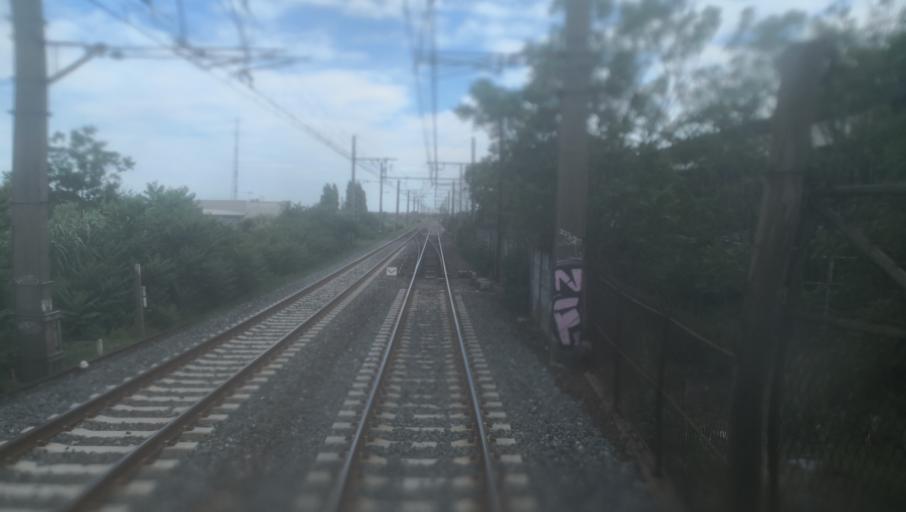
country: FR
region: Languedoc-Roussillon
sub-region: Departement de l'Herault
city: Frontignan
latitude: 43.4414
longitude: 3.7582
